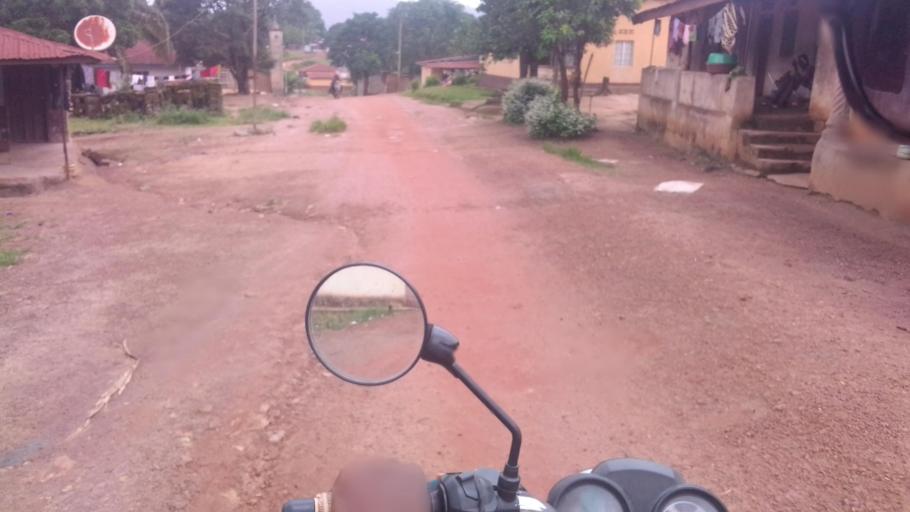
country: SL
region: Eastern Province
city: Kenema
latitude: 7.8689
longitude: -11.1752
